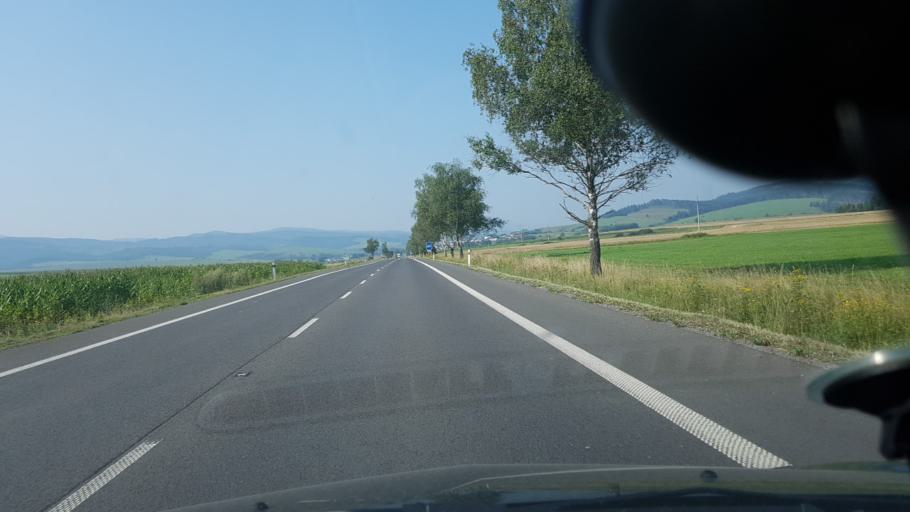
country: SK
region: Zilinsky
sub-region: Okres Zilina
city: Trstena
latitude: 49.3877
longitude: 19.6389
